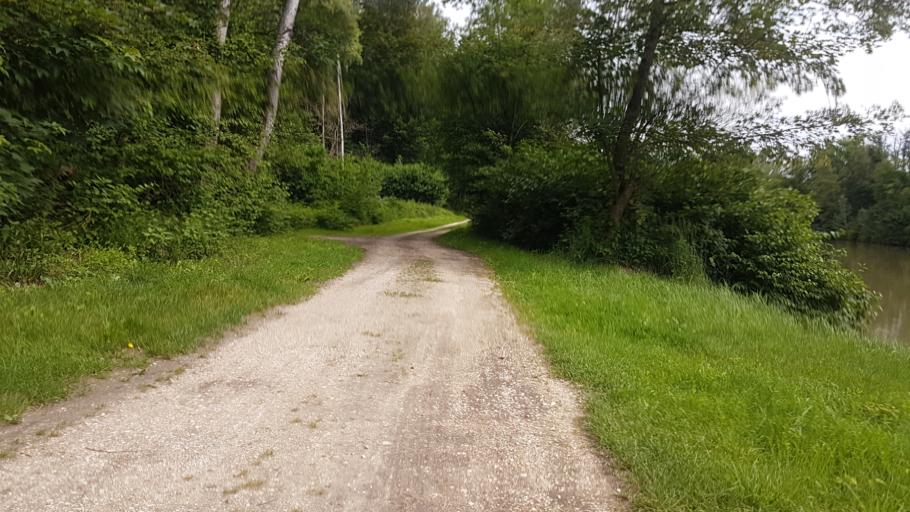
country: DE
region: Bavaria
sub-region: Swabia
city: Gundremmingen
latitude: 48.5174
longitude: 10.3868
